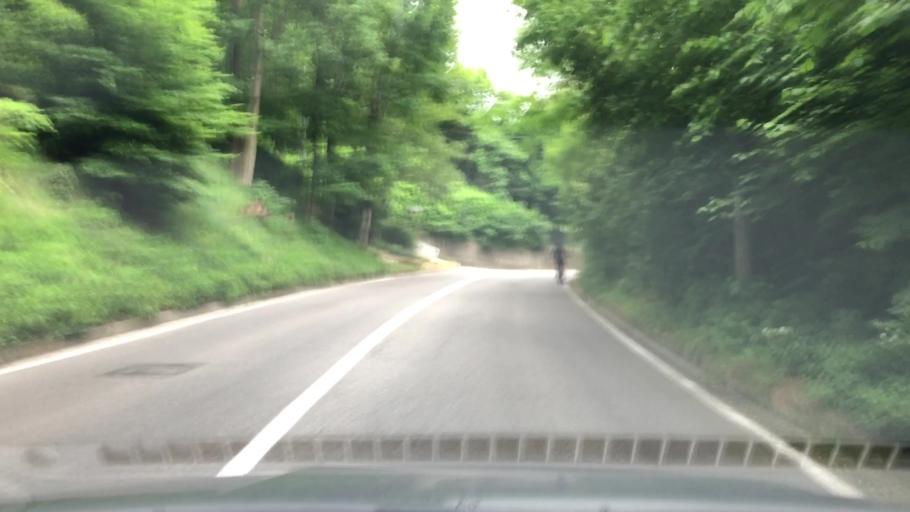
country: IT
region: Lombardy
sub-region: Provincia di Como
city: Vertemate Con Minoprio
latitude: 45.7395
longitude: 9.0670
